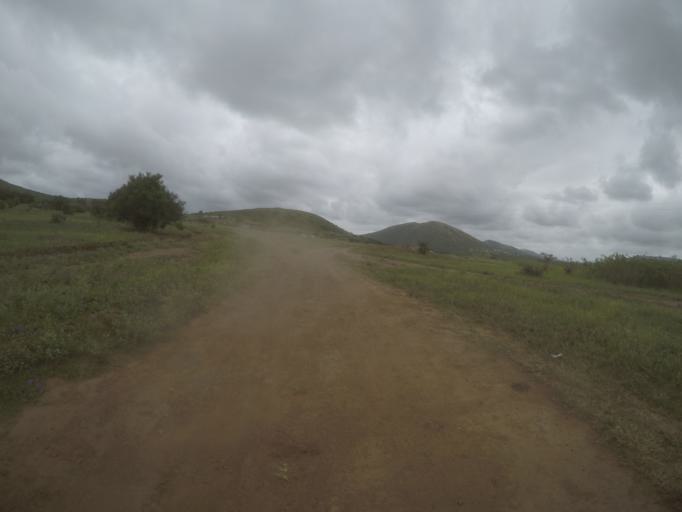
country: ZA
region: KwaZulu-Natal
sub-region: uThungulu District Municipality
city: Empangeni
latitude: -28.6065
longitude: 31.8655
